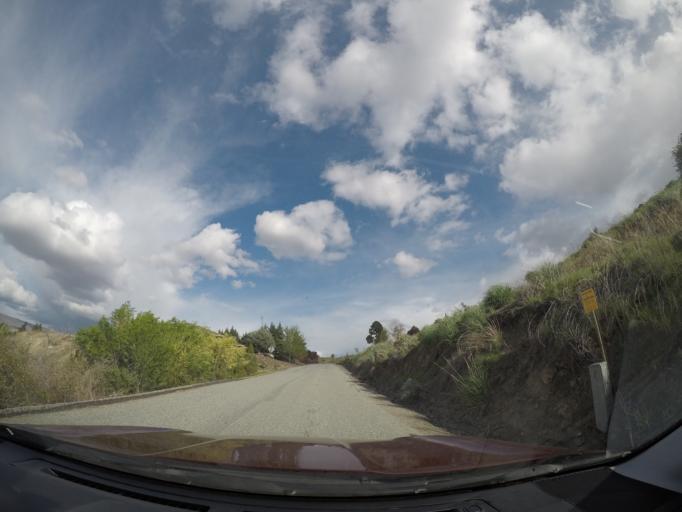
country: US
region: Washington
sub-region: Chelan County
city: Sunnyslope
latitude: 47.4601
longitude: -120.3455
